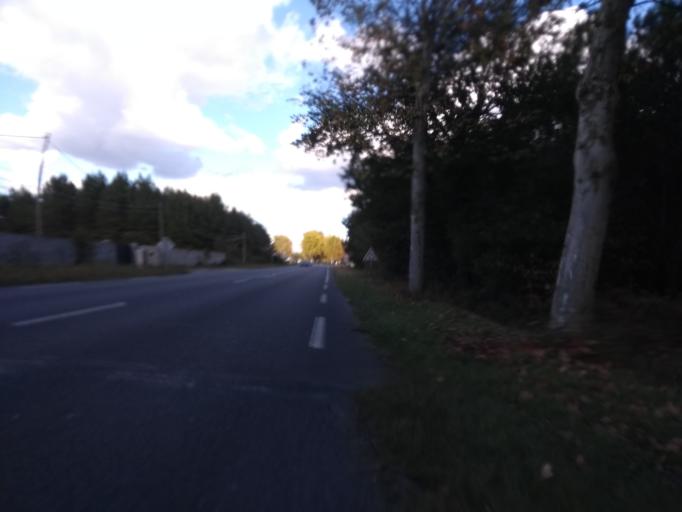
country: FR
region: Aquitaine
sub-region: Departement de la Gironde
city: Saint-Aubin-de-Medoc
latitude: 44.6995
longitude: -0.7073
